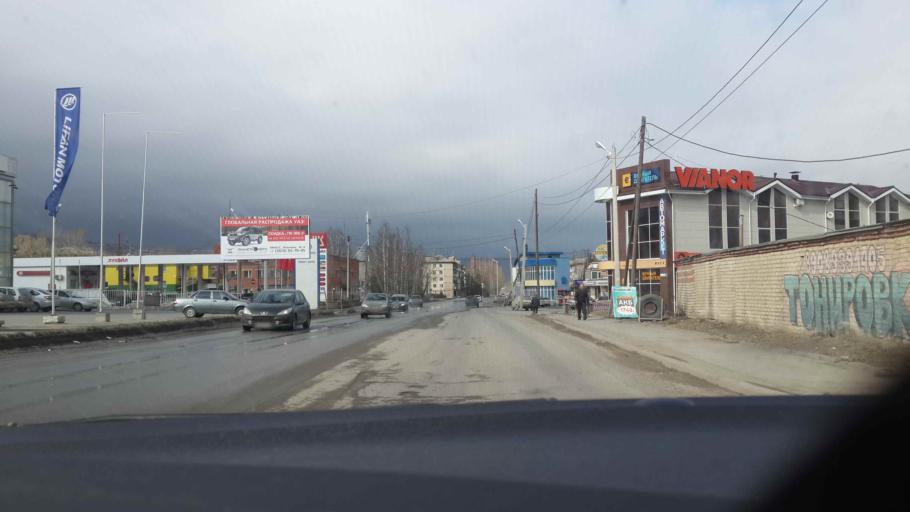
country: RU
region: Chelyabinsk
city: Zlatoust
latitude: 55.1380
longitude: 59.6734
